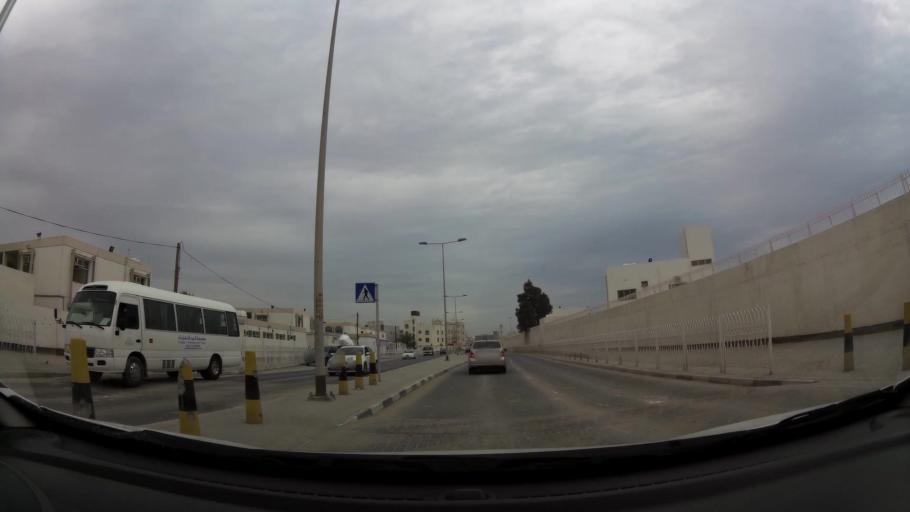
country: BH
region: Northern
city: Sitrah
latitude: 26.1550
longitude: 50.6199
